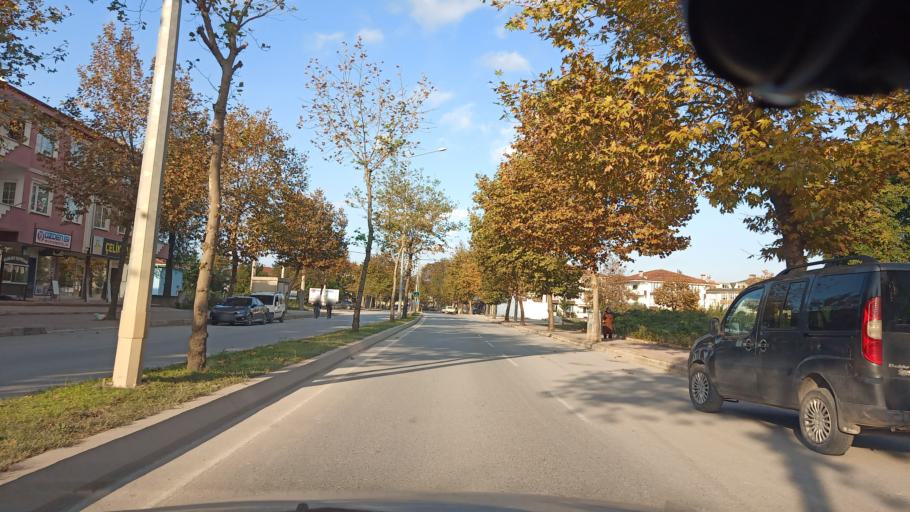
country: TR
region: Sakarya
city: Karasu
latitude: 41.0999
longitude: 30.6894
